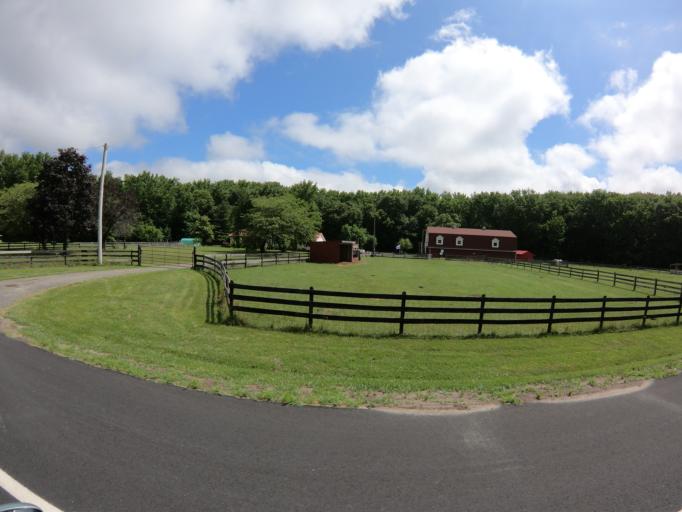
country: US
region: Maryland
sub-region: Caroline County
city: Greensboro
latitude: 39.0430
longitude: -75.8051
